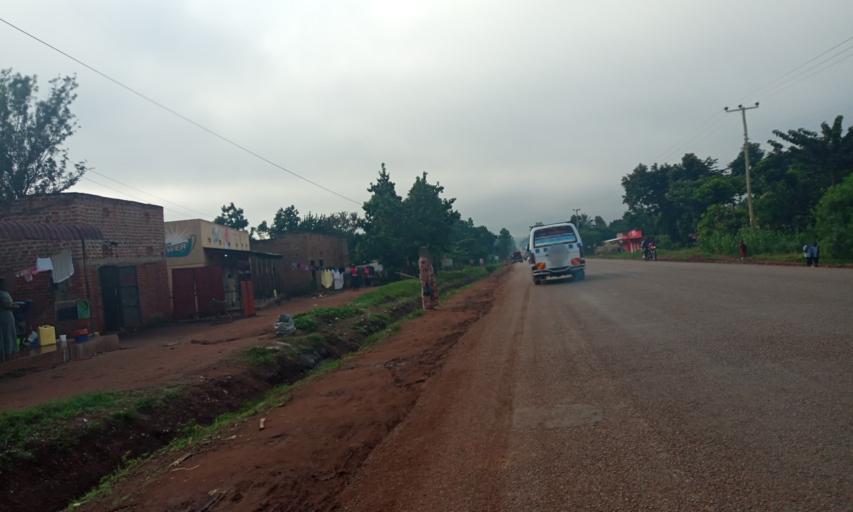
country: UG
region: Eastern Region
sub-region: Mbale District
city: Mbale
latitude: 1.1207
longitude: 34.1695
